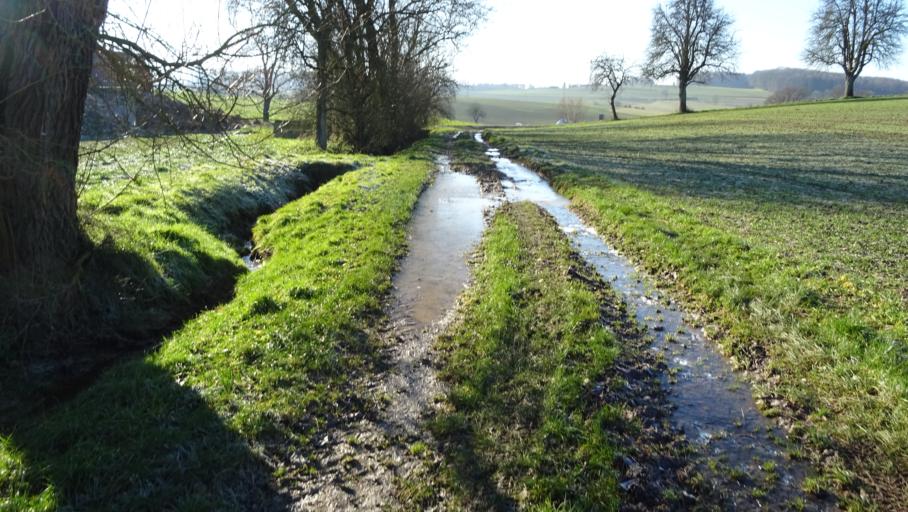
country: DE
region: Baden-Wuerttemberg
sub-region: Karlsruhe Region
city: Mosbach
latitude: 49.3412
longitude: 9.1789
